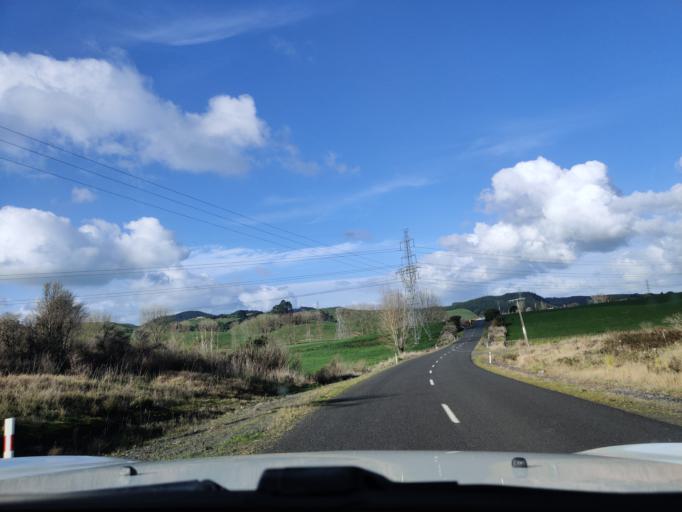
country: NZ
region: Waikato
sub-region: Waikato District
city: Te Kauwhata
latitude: -37.2830
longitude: 175.2070
